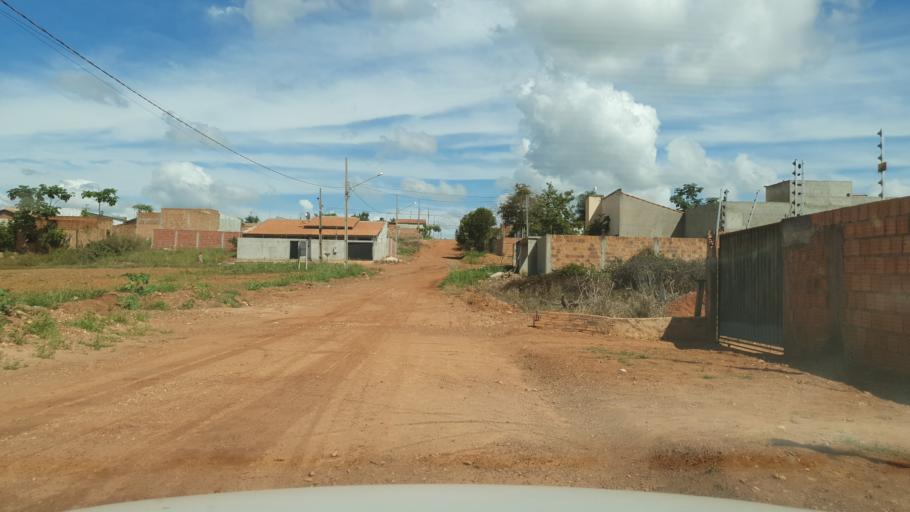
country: BR
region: Mato Grosso
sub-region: Pontes E Lacerda
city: Pontes e Lacerda
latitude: -15.2514
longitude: -59.3128
